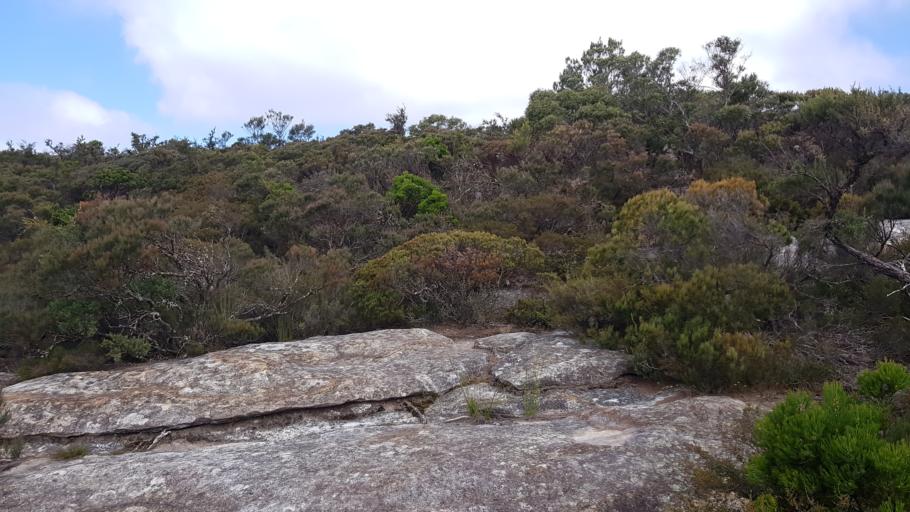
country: AU
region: New South Wales
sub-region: Blue Mountains Municipality
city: Katoomba
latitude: -33.9831
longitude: 150.1308
